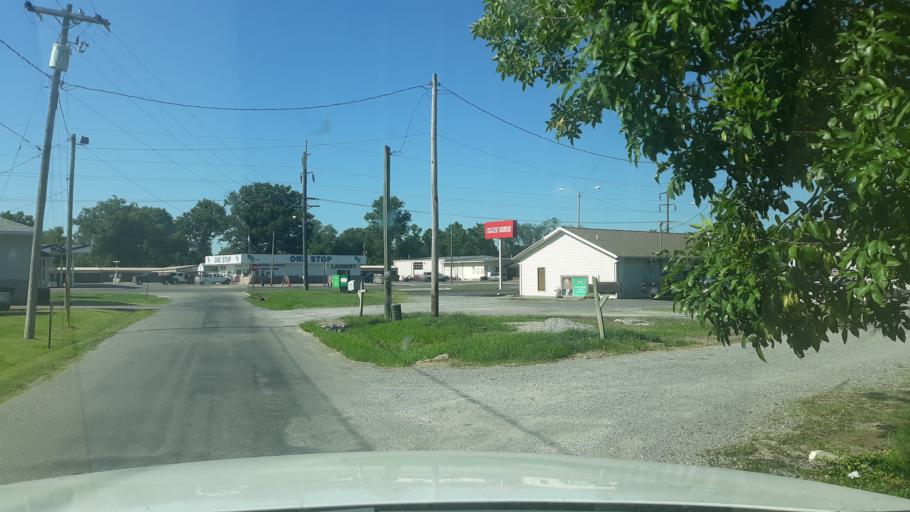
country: US
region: Illinois
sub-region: Saline County
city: Eldorado
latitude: 37.8068
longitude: -88.4384
